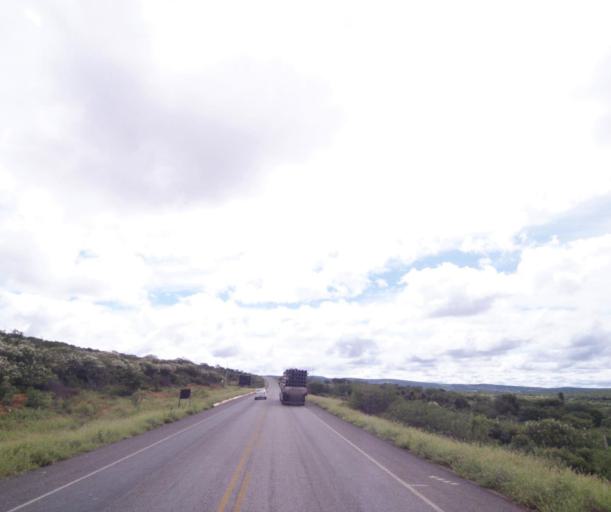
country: BR
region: Bahia
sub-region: Brumado
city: Brumado
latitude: -14.2184
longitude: -41.6624
